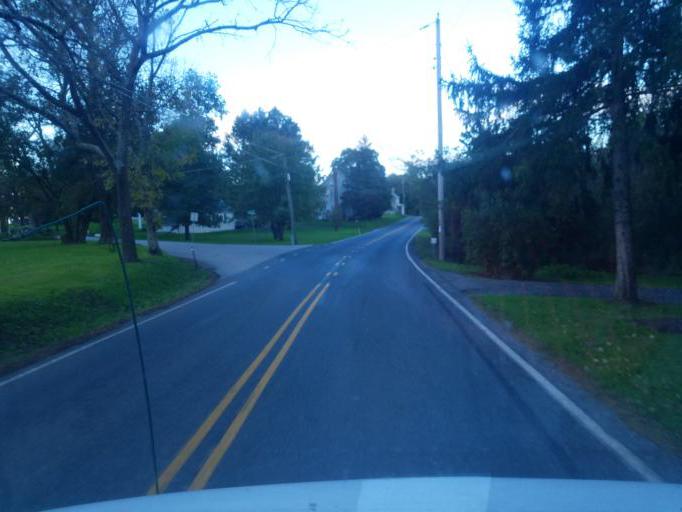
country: US
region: Pennsylvania
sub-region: Adams County
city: New Oxford
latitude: 39.9006
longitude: -77.0985
